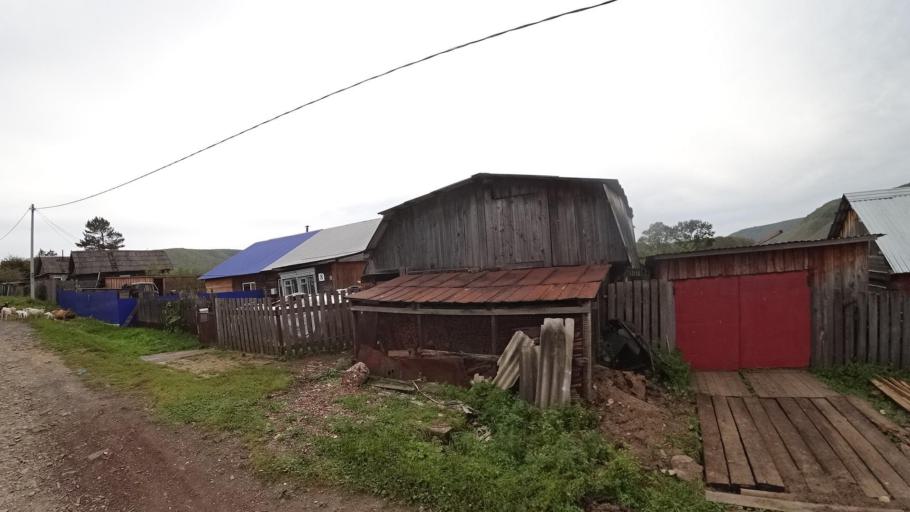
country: RU
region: Jewish Autonomous Oblast
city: Khingansk
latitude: 49.1301
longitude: 131.2011
